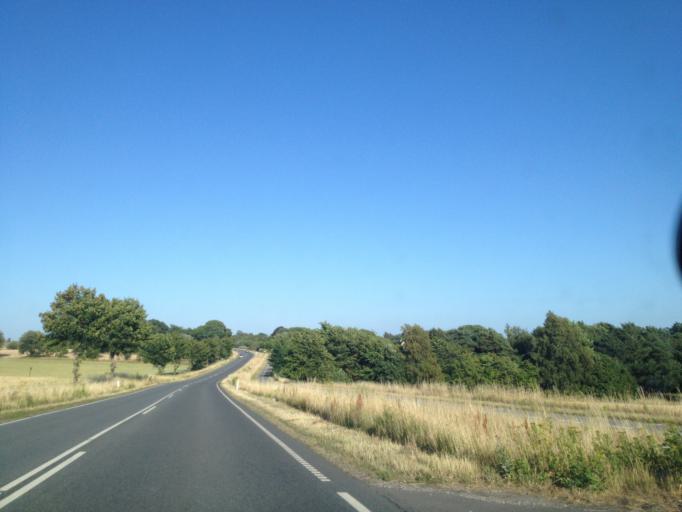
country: DK
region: Capital Region
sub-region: Gribskov Kommune
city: Helsinge
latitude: 56.0170
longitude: 12.1343
